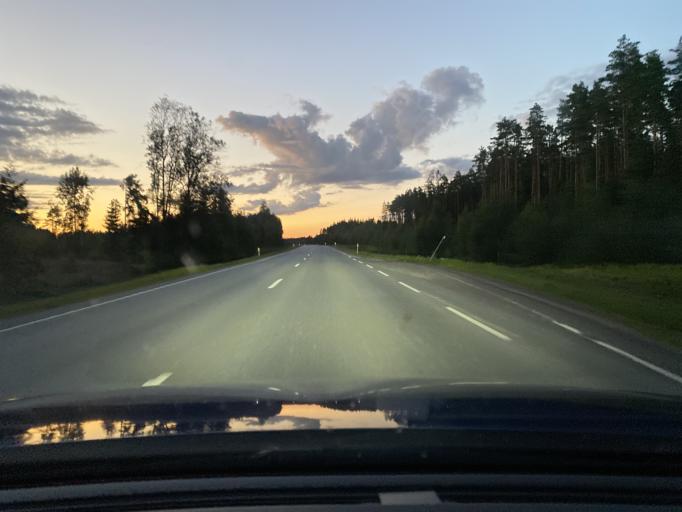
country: FI
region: Varsinais-Suomi
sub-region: Loimaa
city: Oripaeae
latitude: 60.8851
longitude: 22.7019
